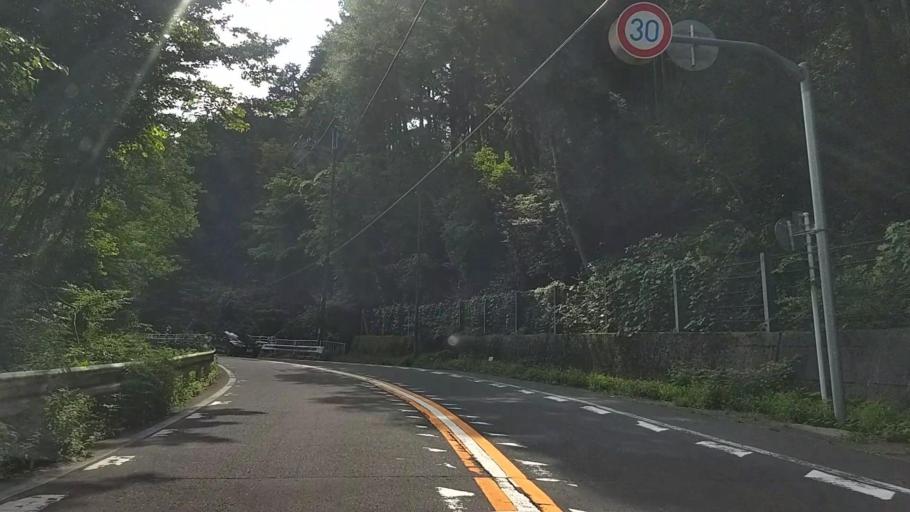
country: JP
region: Tokyo
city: Hachioji
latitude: 35.6194
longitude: 139.2327
